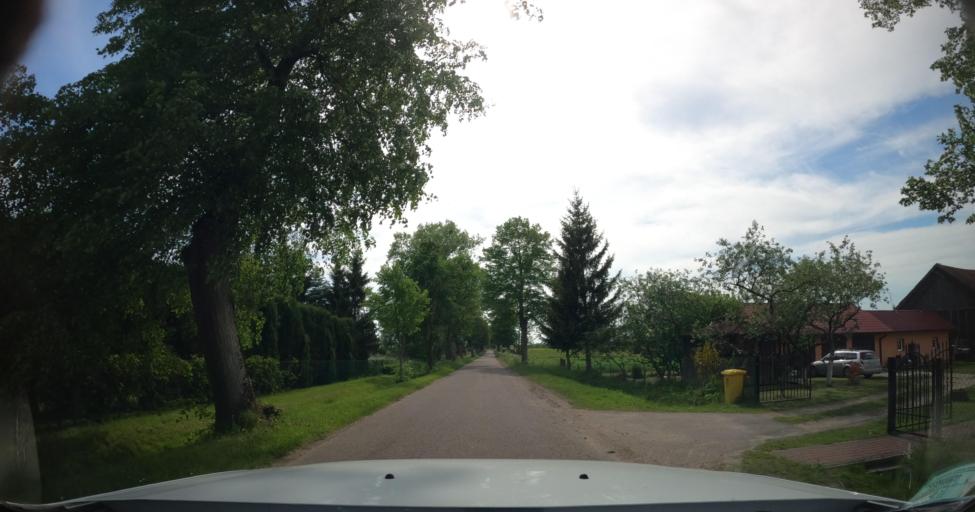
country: PL
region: Warmian-Masurian Voivodeship
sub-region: Powiat lidzbarski
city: Lubomino
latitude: 54.0872
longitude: 20.2894
